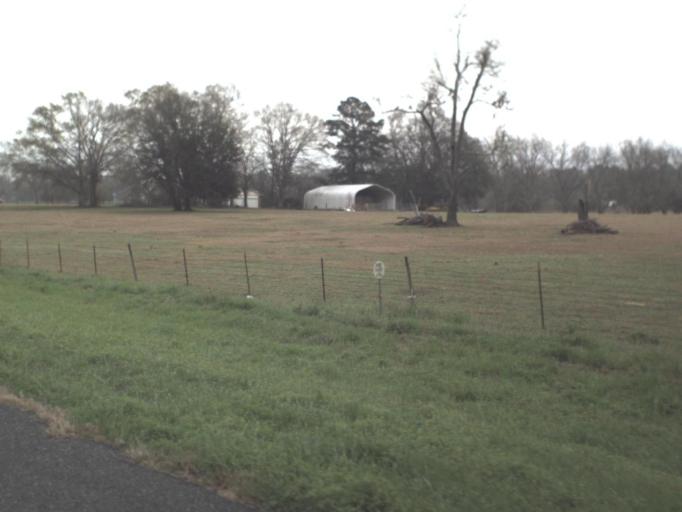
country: US
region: Florida
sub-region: Jefferson County
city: Monticello
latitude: 30.4073
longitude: -83.9895
